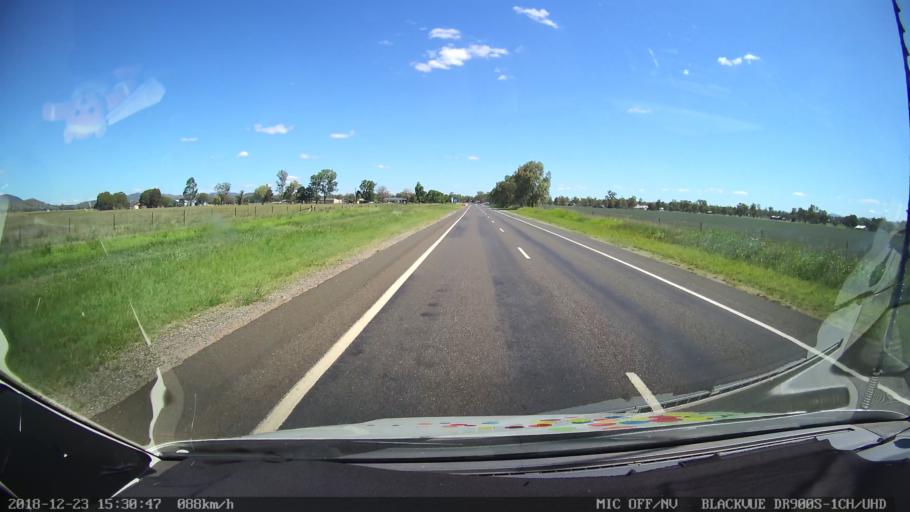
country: AU
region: New South Wales
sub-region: Tamworth Municipality
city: East Tamworth
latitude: -30.9636
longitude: 150.8663
